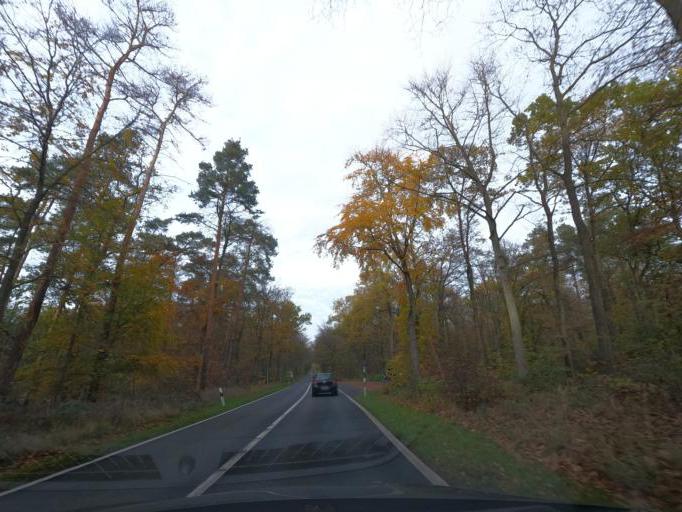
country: DE
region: Lower Saxony
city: Braunschweig
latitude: 52.3078
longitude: 10.5695
